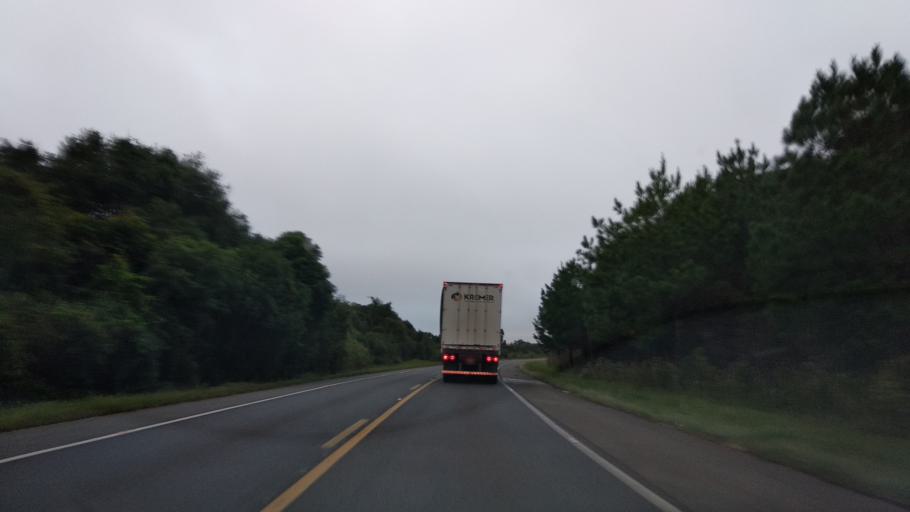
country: BR
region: Santa Catarina
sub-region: Campos Novos
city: Campos Novos
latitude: -27.3764
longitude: -51.0910
